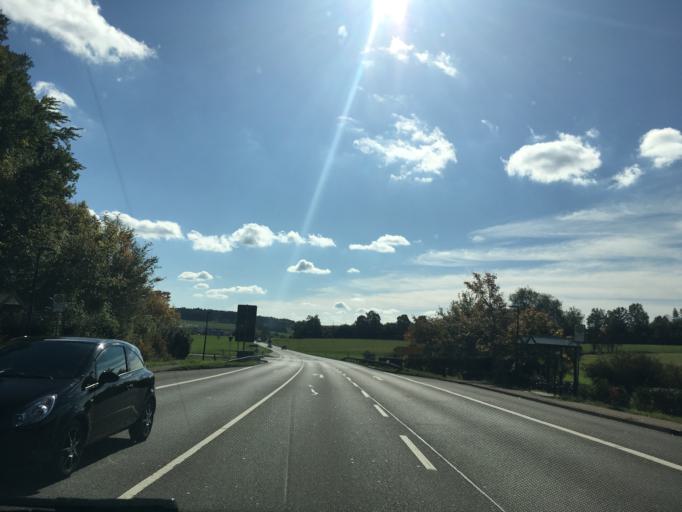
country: DE
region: Baden-Wuerttemberg
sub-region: Karlsruhe Region
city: Althengstett
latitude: 48.7347
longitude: 8.7899
